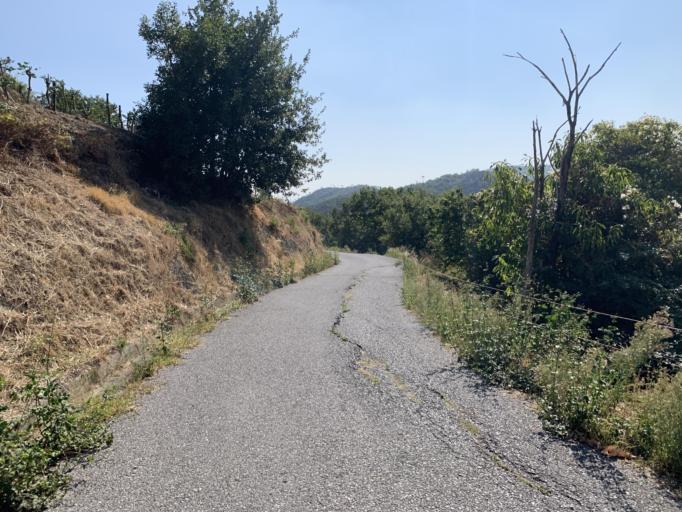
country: IT
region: Liguria
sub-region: Provincia di Savona
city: Magliolo
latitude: 44.1891
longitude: 8.2417
